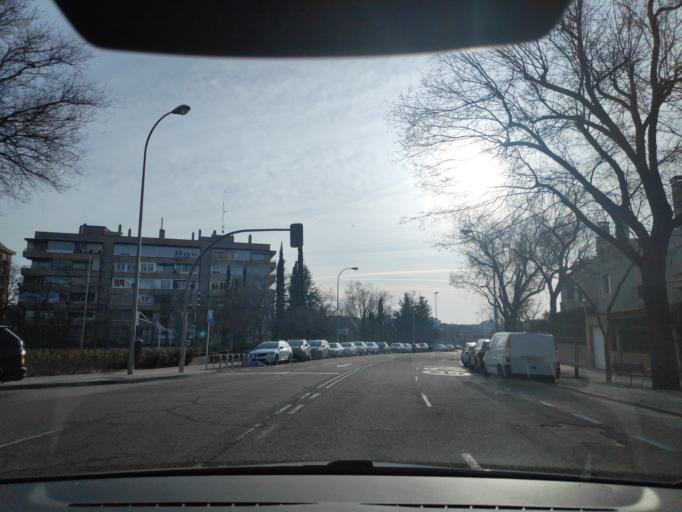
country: ES
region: Madrid
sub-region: Provincia de Madrid
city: Chamartin
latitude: 40.4600
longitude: -3.6697
